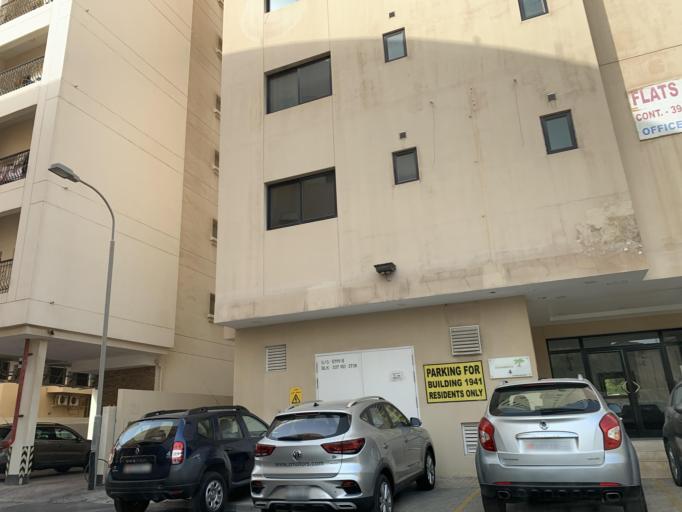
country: BH
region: Manama
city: Manama
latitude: 26.2054
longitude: 50.5919
